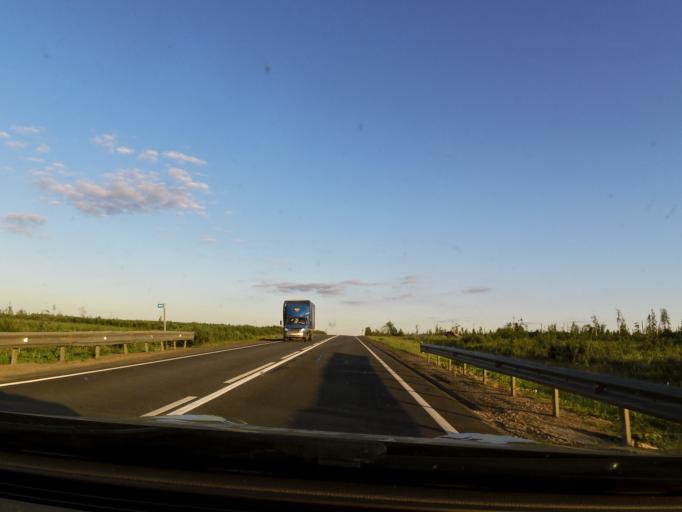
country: RU
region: Jaroslavl
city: Prechistoye
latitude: 58.5937
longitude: 40.3445
